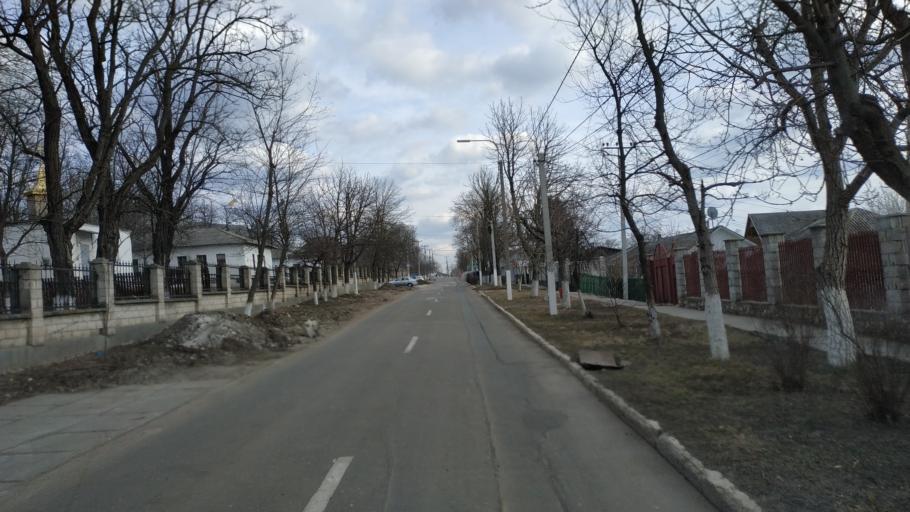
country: MD
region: Hincesti
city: Hincesti
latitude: 46.8336
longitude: 28.5808
